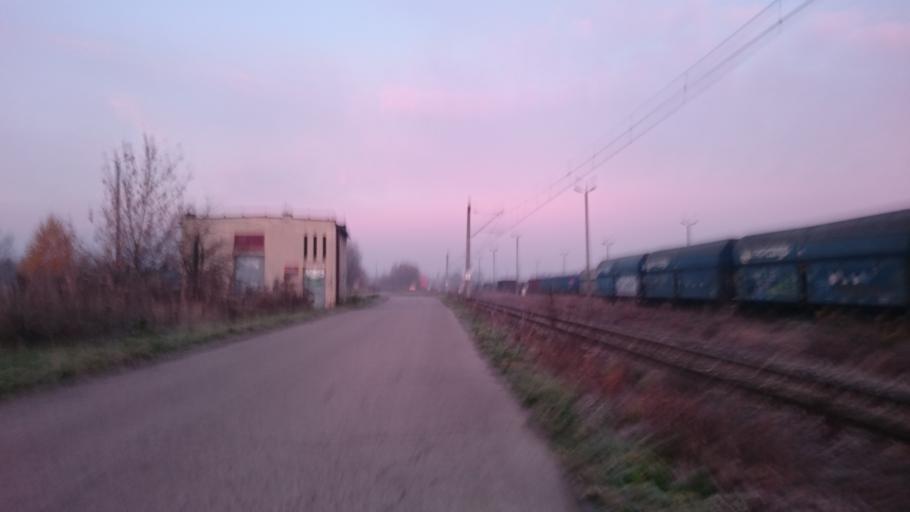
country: PL
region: Lesser Poland Voivodeship
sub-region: Powiat wielicki
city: Czarnochowice
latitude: 50.0265
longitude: 20.0123
